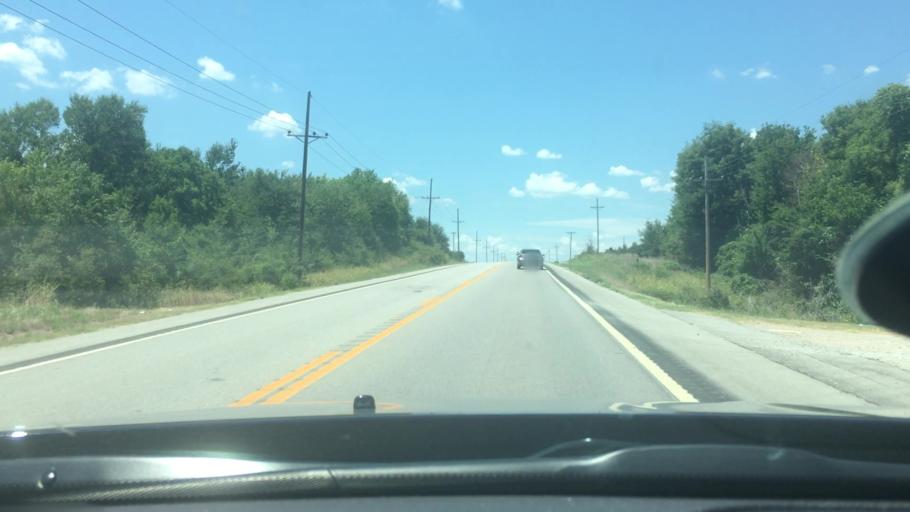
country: US
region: Oklahoma
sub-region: Bryan County
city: Durant
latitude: 33.9975
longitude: -96.2604
